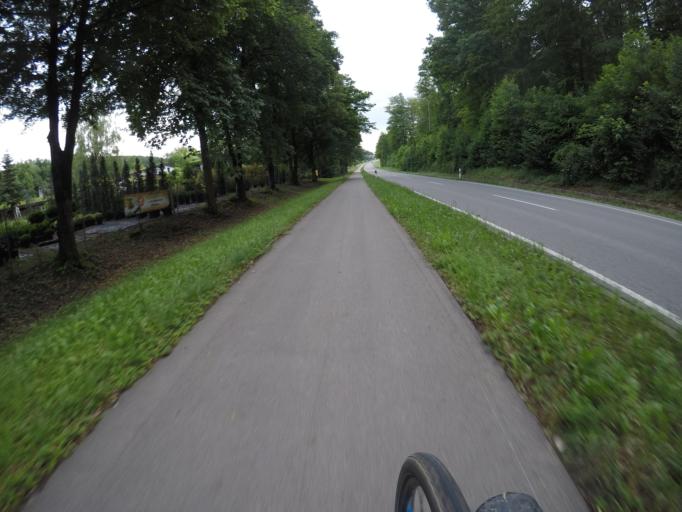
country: DE
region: Baden-Wuerttemberg
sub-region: Regierungsbezirk Stuttgart
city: Frickenhausen
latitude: 48.5826
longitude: 9.3410
